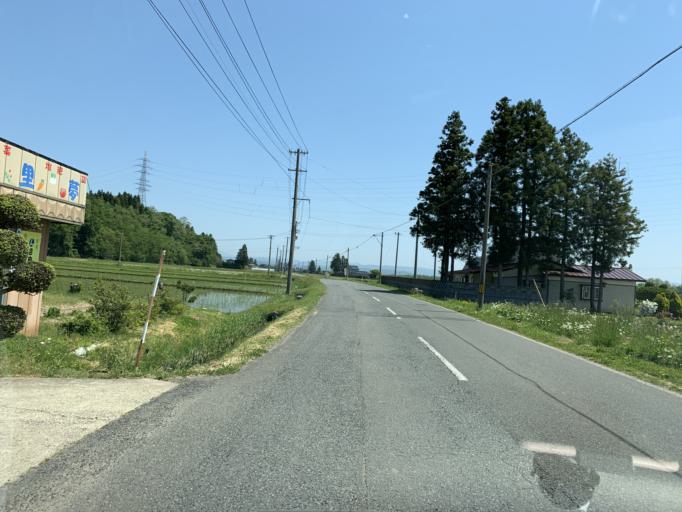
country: JP
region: Iwate
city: Mizusawa
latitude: 39.1625
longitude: 141.0773
